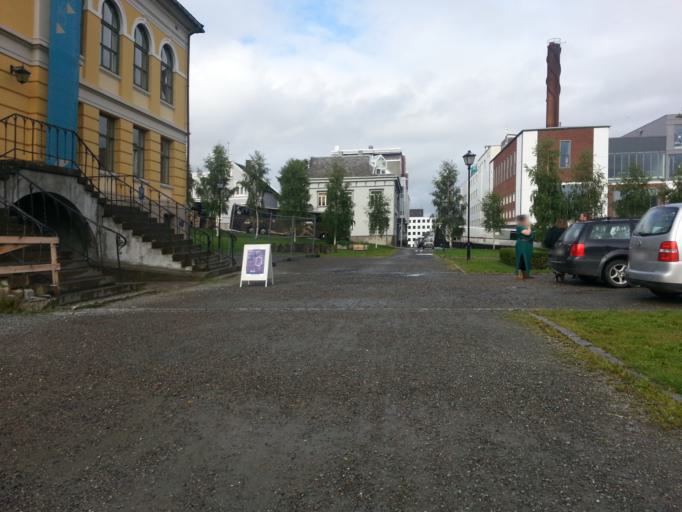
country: NO
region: Troms
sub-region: Tromso
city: Tromso
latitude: 69.6454
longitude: 18.9473
